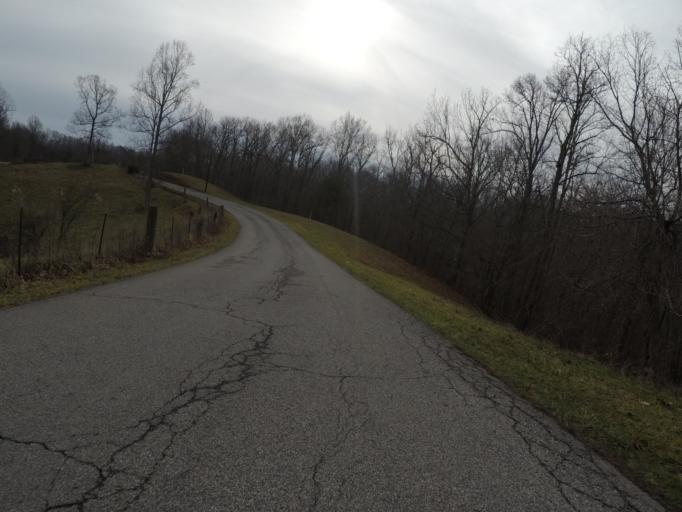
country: US
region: West Virginia
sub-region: Wayne County
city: Lavalette
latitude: 38.3557
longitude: -82.4115
